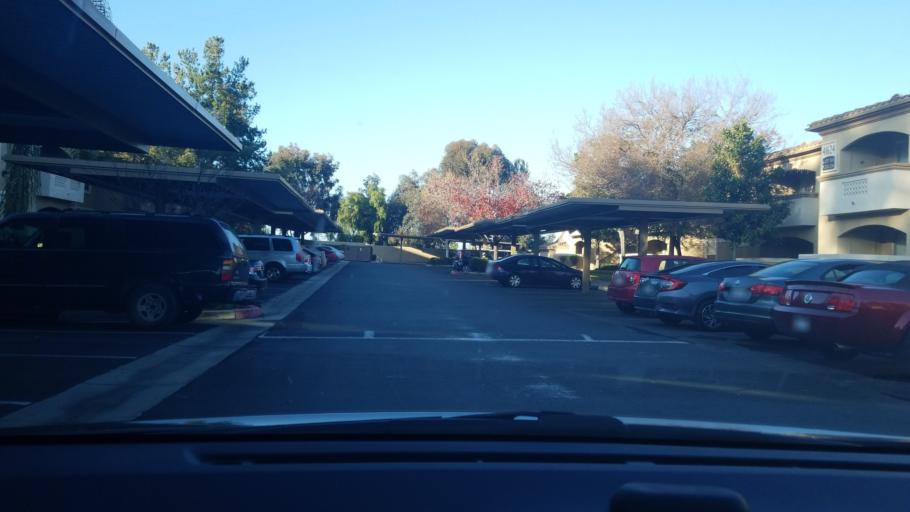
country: US
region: California
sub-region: Riverside County
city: Temecula
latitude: 33.5197
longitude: -117.1503
